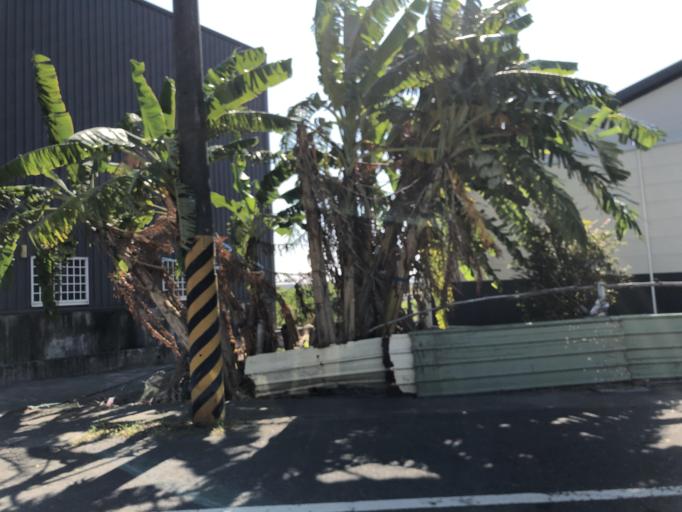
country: TW
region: Taiwan
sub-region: Tainan
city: Tainan
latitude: 23.0046
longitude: 120.2750
